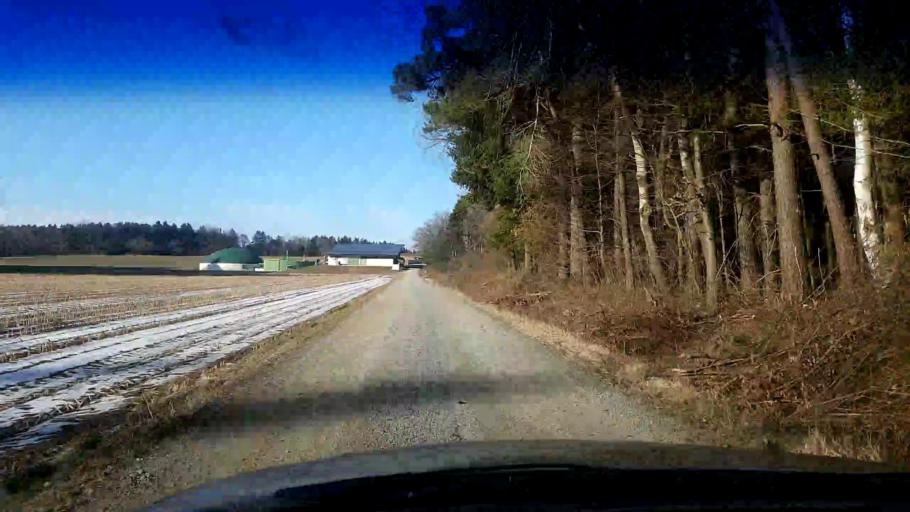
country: DE
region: Bavaria
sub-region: Upper Franconia
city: Aufsess
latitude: 49.9214
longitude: 11.1998
